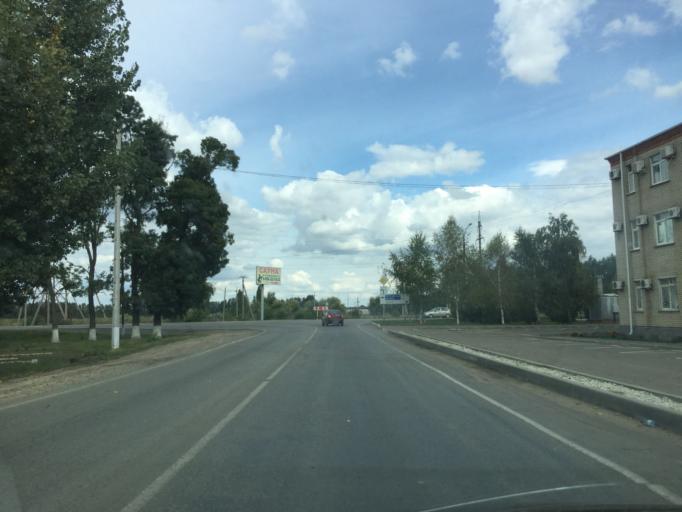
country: RU
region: Krasnodarskiy
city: Sovkhoznyy
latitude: 45.2850
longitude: 38.0986
